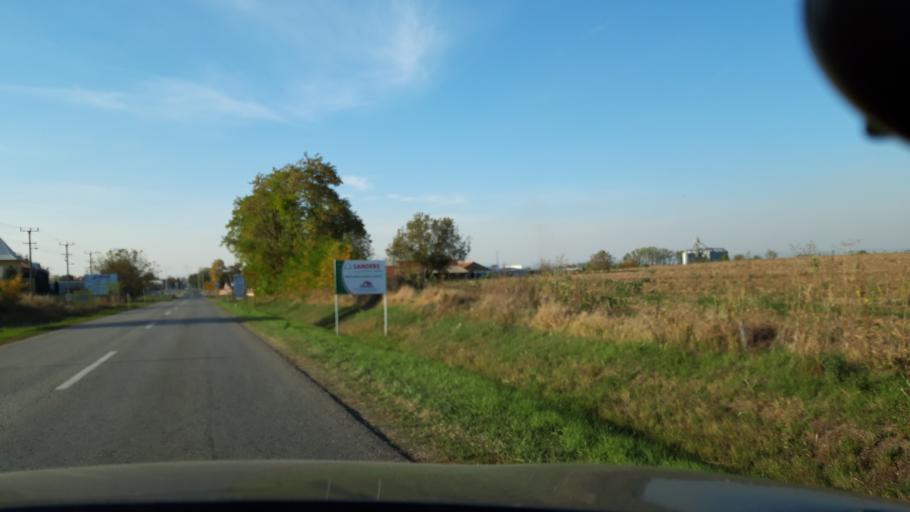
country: RS
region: Autonomna Pokrajina Vojvodina
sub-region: Sremski Okrug
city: Ruma
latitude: 44.9998
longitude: 19.8469
